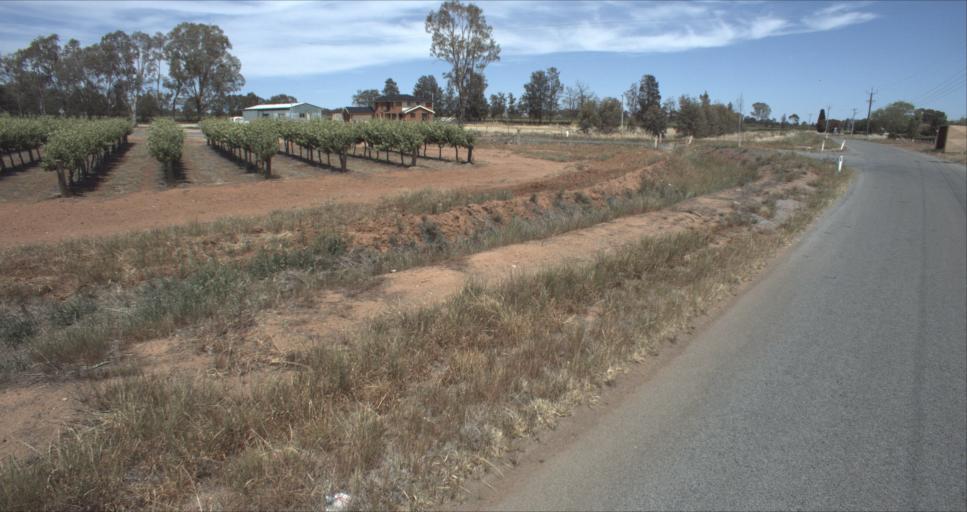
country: AU
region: New South Wales
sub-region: Leeton
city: Leeton
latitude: -34.5681
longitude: 146.4443
